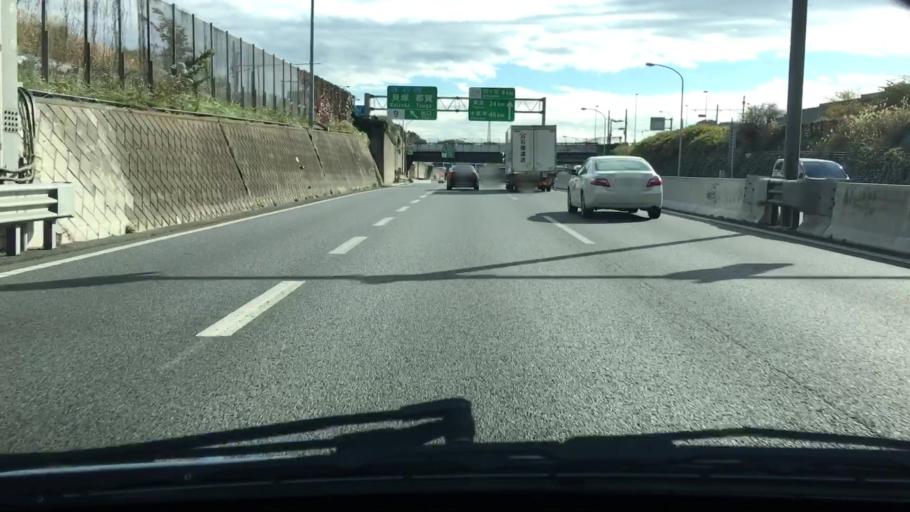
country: JP
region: Chiba
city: Chiba
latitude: 35.6258
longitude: 140.1391
